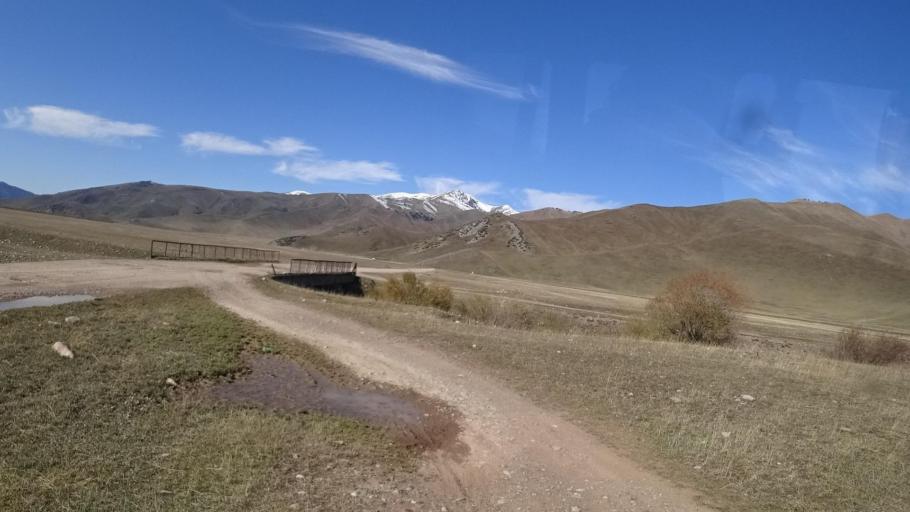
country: KZ
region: Almaty Oblysy
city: Kegen
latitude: 42.7469
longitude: 78.9913
